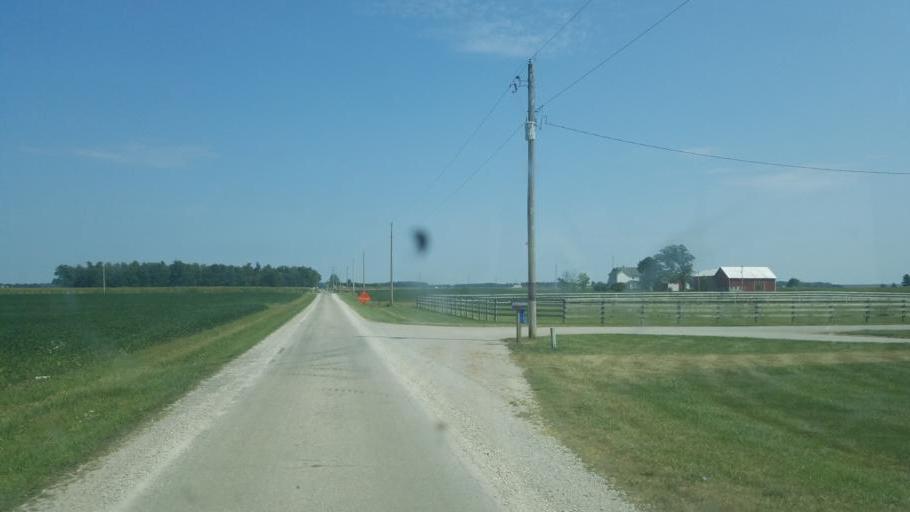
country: US
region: Ohio
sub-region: Crawford County
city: Bucyrus
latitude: 40.9361
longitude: -82.8855
